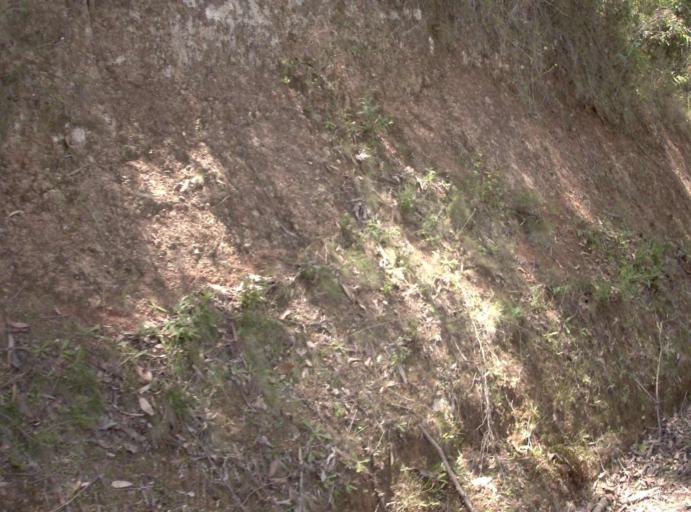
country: AU
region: New South Wales
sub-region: Bombala
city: Bombala
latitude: -37.4714
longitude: 148.9287
